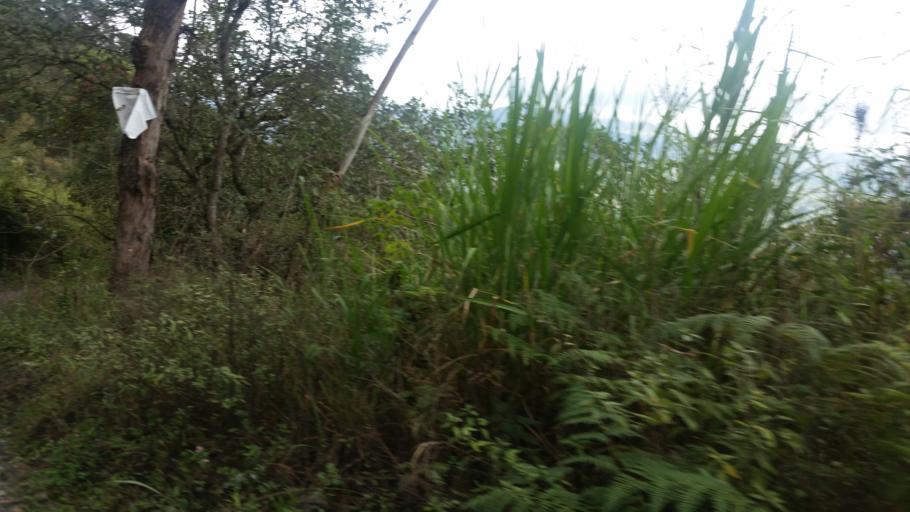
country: CO
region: Cundinamarca
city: Choachi
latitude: 4.5144
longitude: -73.9300
